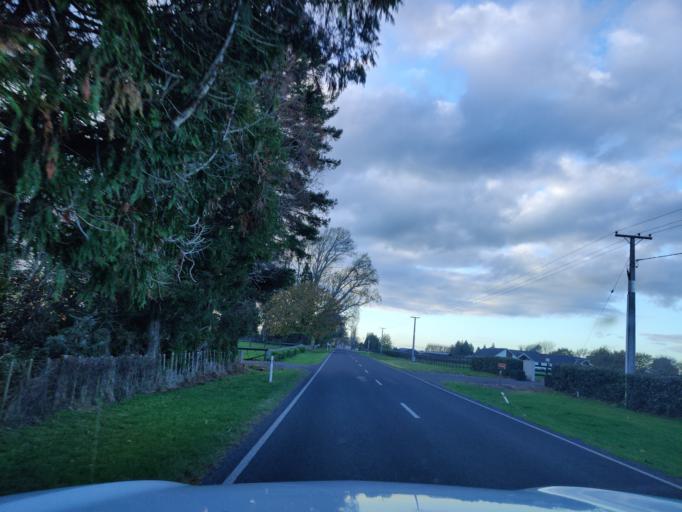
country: NZ
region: Waikato
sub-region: Waipa District
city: Cambridge
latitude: -37.8492
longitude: 175.4390
